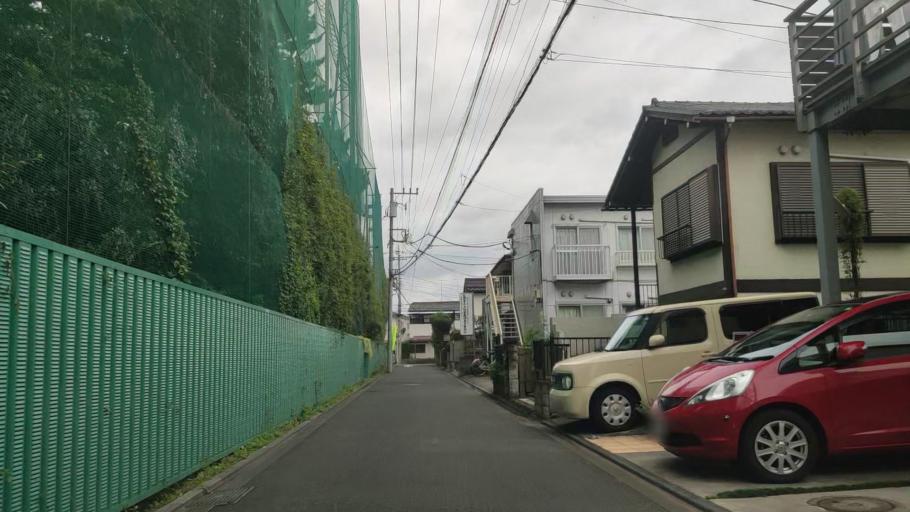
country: JP
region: Tokyo
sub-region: Machida-shi
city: Machida
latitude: 35.5125
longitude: 139.4386
